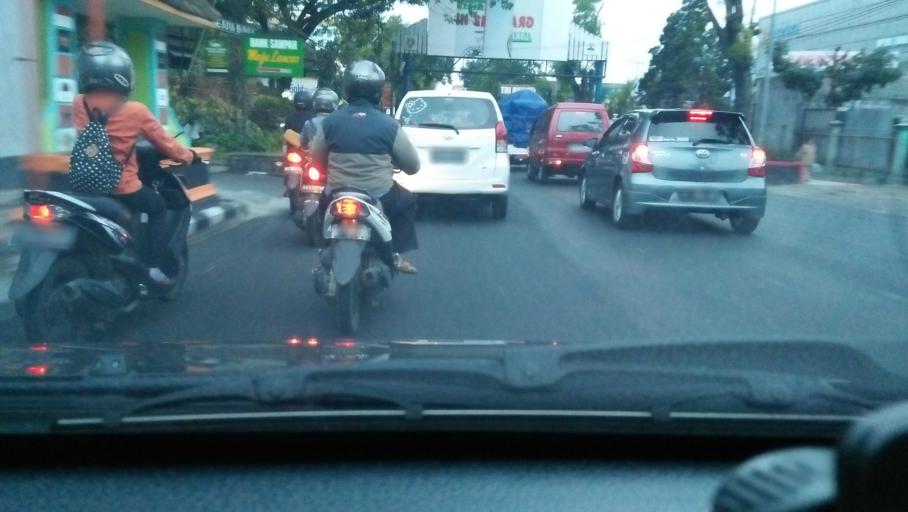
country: ID
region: Central Java
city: Mertoyudan
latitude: -7.5013
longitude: 110.2236
